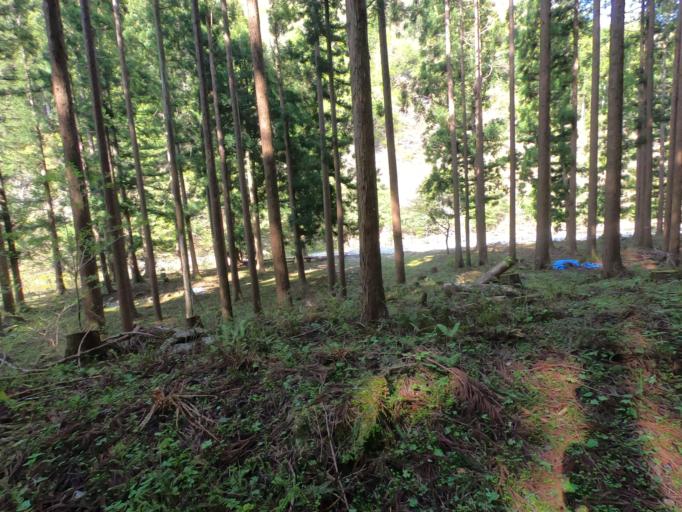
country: JP
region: Fukui
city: Obama
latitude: 35.3072
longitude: 135.7185
